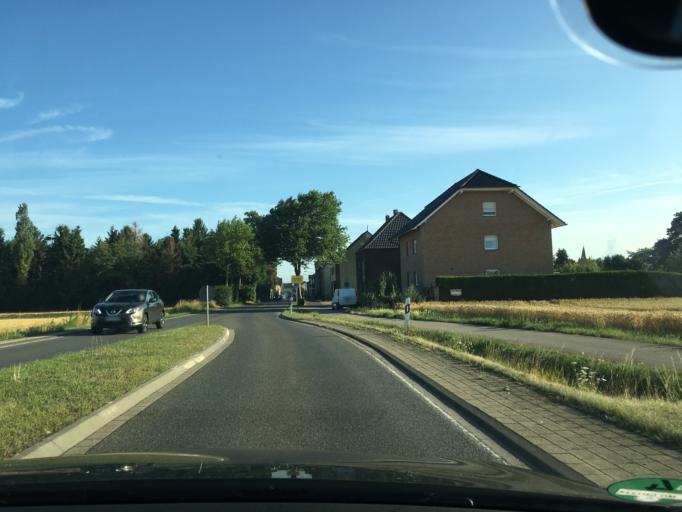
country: DE
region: North Rhine-Westphalia
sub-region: Regierungsbezirk Koln
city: Dueren
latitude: 50.8327
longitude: 6.4910
